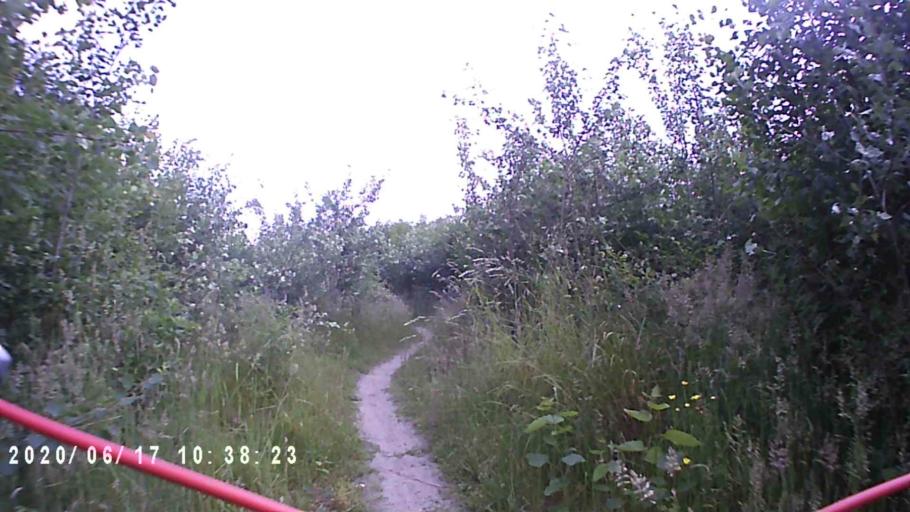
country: NL
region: Groningen
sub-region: Gemeente De Marne
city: Ulrum
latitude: 53.4007
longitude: 6.2332
